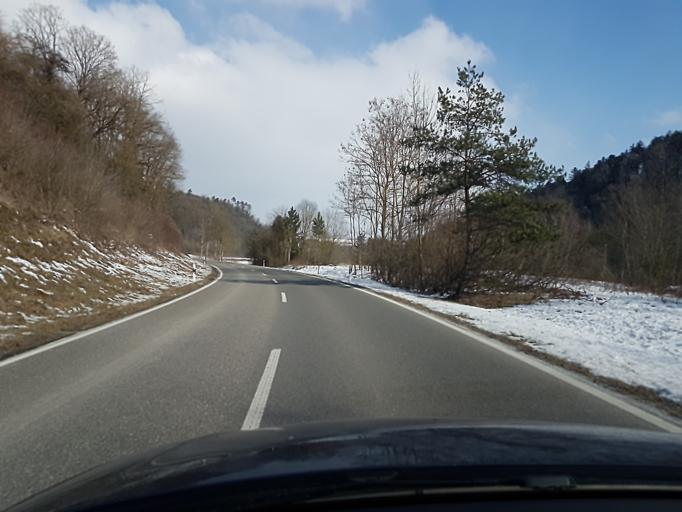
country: DE
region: Baden-Wuerttemberg
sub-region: Freiburg Region
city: Muhlheim am Bach
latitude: 48.3755
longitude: 8.6674
